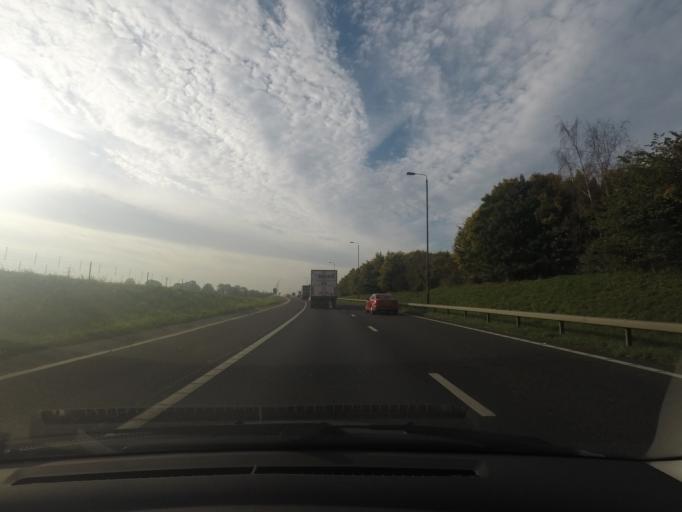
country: GB
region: England
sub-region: City and Borough of Leeds
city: Aberford
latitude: 53.8525
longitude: -1.3429
